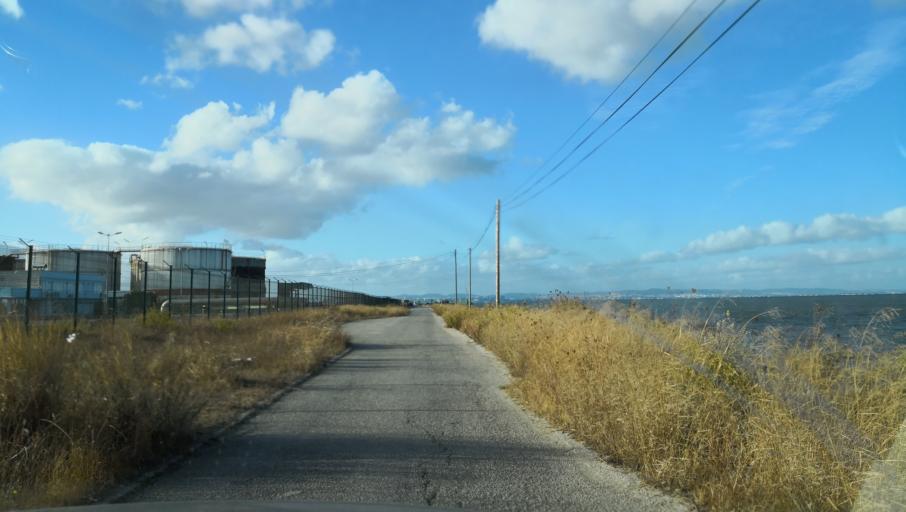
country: PT
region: Setubal
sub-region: Barreiro
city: Barreiro
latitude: 38.6811
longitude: -9.0566
